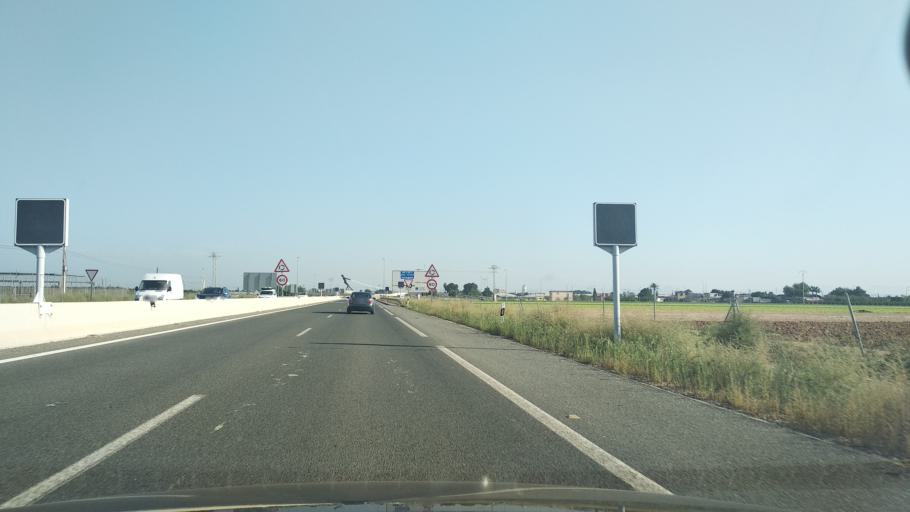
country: ES
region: Murcia
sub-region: Murcia
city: San Javier
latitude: 37.8235
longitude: -0.8516
